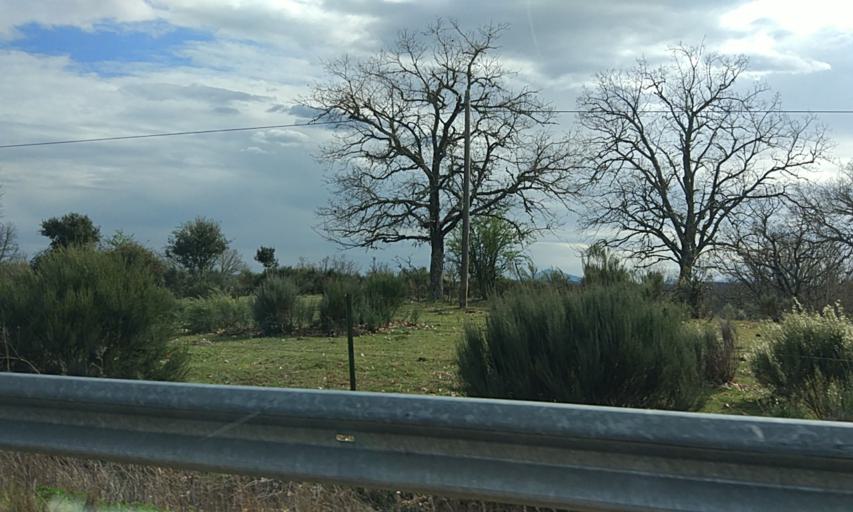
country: ES
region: Castille and Leon
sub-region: Provincia de Salamanca
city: Robleda
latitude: 40.4314
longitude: -6.6043
